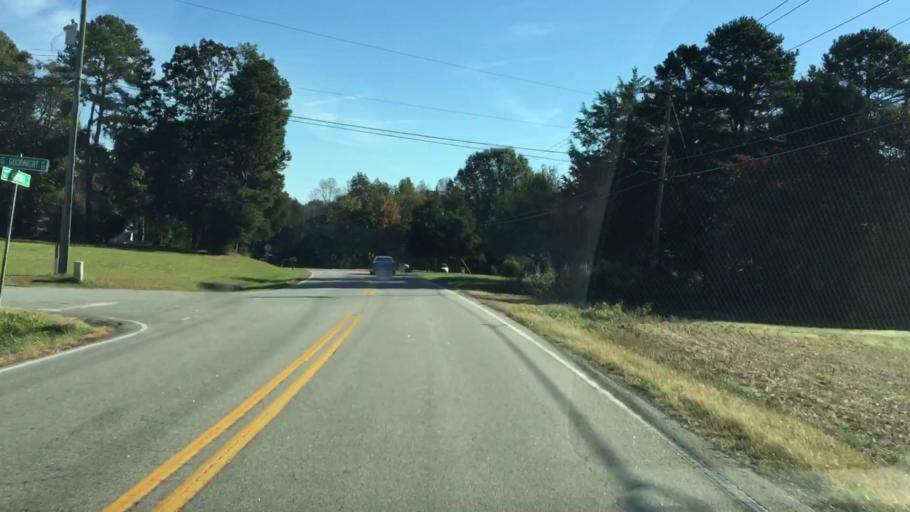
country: US
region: North Carolina
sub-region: Rowan County
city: China Grove
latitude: 35.6488
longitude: -80.6138
